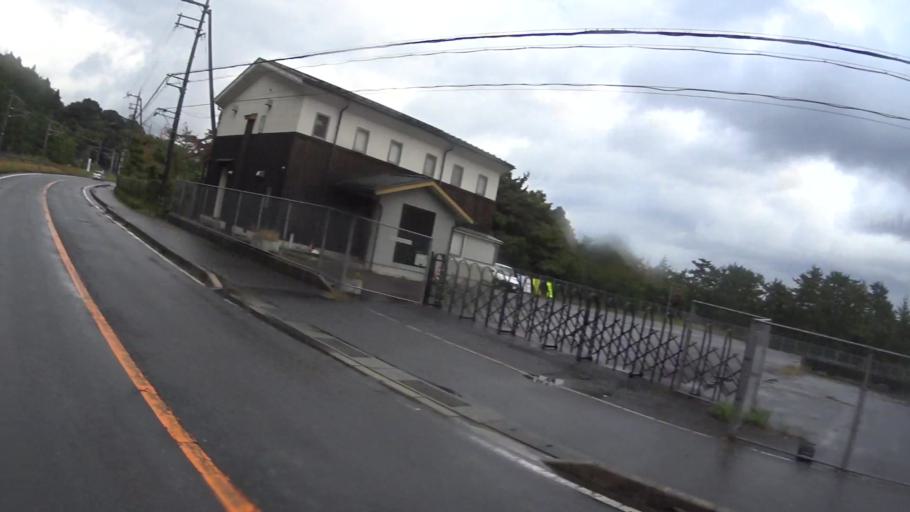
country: JP
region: Kyoto
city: Miyazu
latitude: 35.5514
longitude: 135.1854
